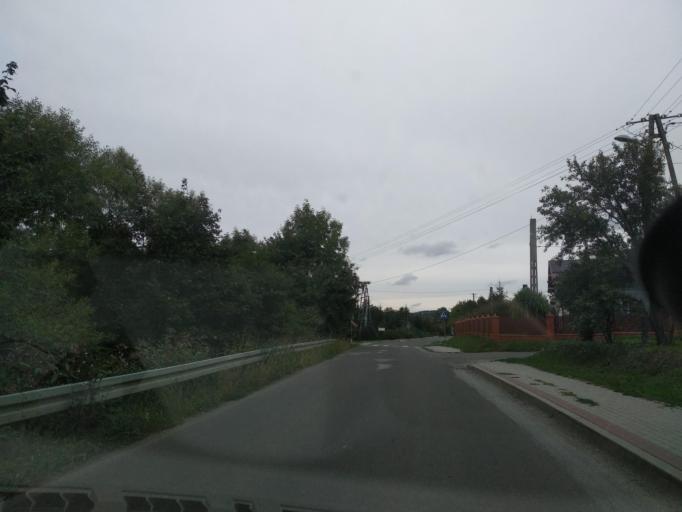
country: PL
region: Subcarpathian Voivodeship
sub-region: Powiat krosnienski
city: Iwonicz-Zdroj
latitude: 49.5740
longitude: 21.7538
